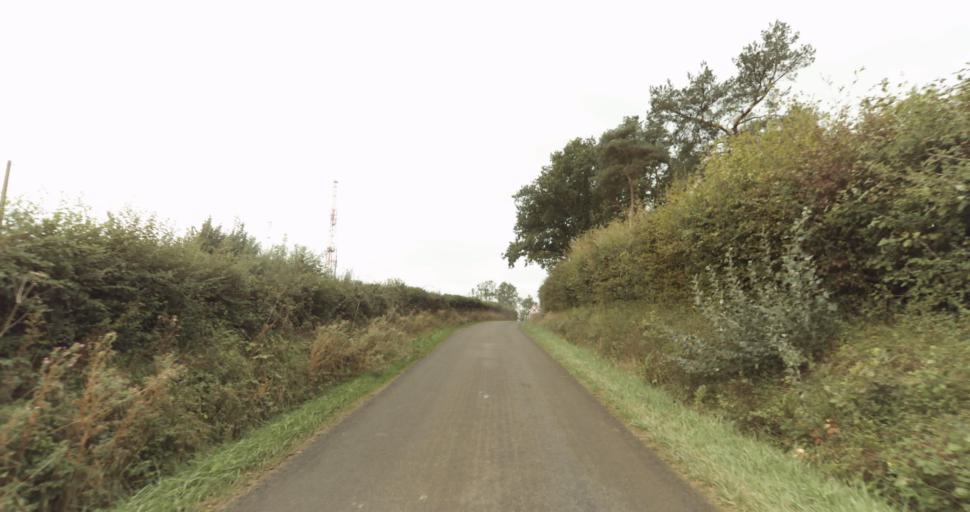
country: FR
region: Lower Normandy
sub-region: Departement de l'Orne
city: Gace
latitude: 48.7180
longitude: 0.3201
